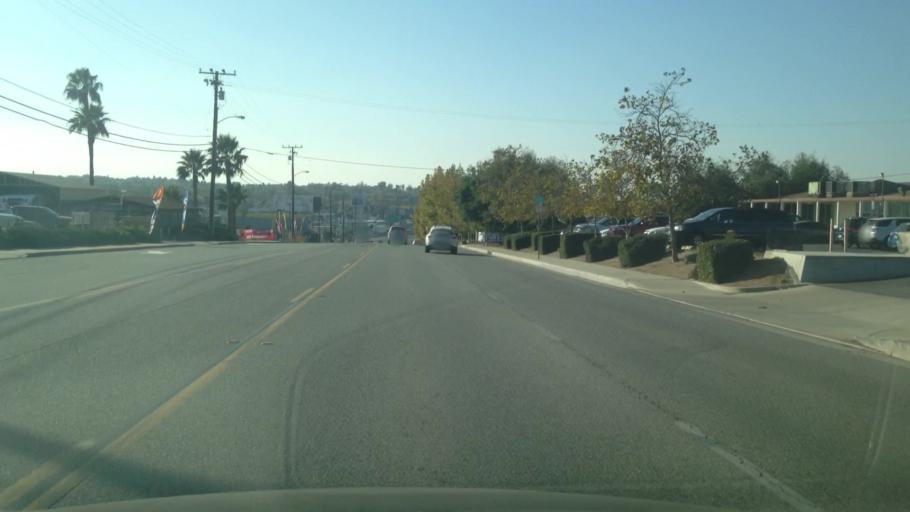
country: US
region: California
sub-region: Riverside County
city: March Air Force Base
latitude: 33.9466
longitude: -117.2930
